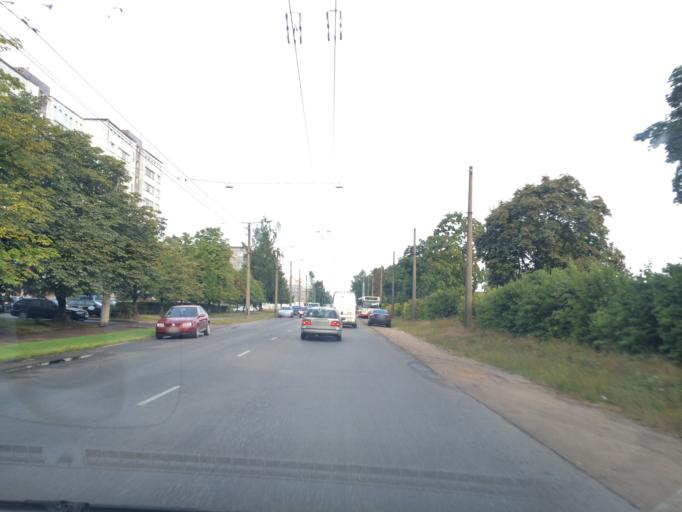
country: LV
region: Kekava
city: Kekava
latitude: 56.9032
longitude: 24.2129
